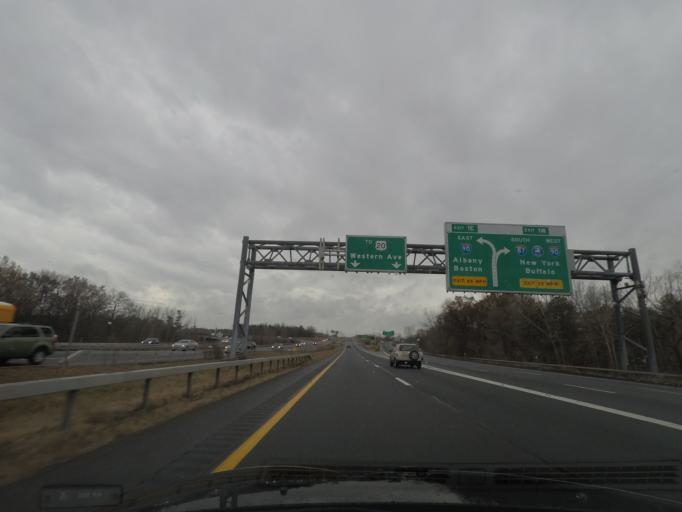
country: US
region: New York
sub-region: Albany County
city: Colonie
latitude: 42.7003
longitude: -73.8355
